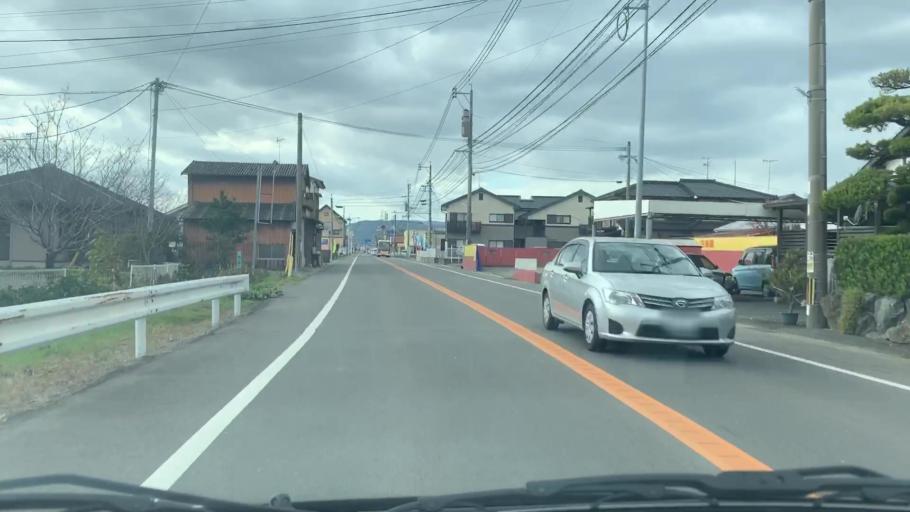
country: JP
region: Saga Prefecture
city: Saga-shi
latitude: 33.2503
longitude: 130.2348
